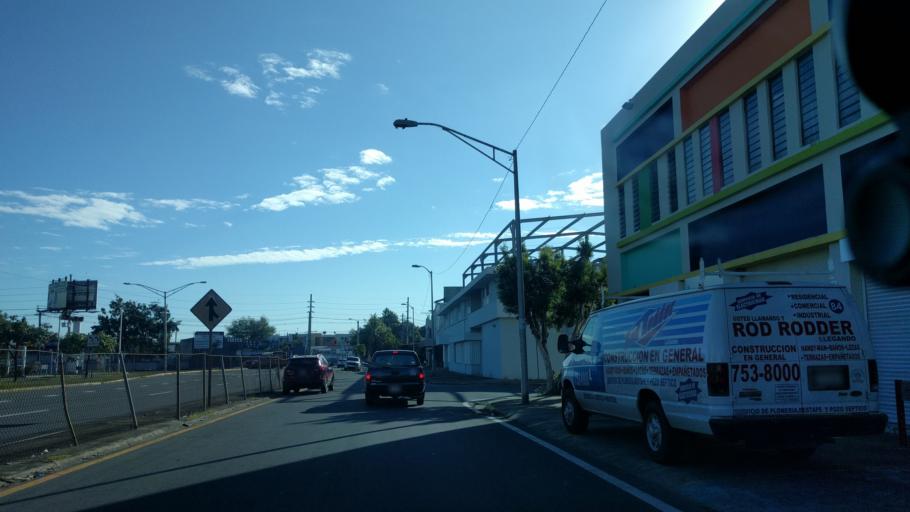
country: PR
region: San Juan
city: San Juan
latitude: 18.4253
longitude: -66.0492
